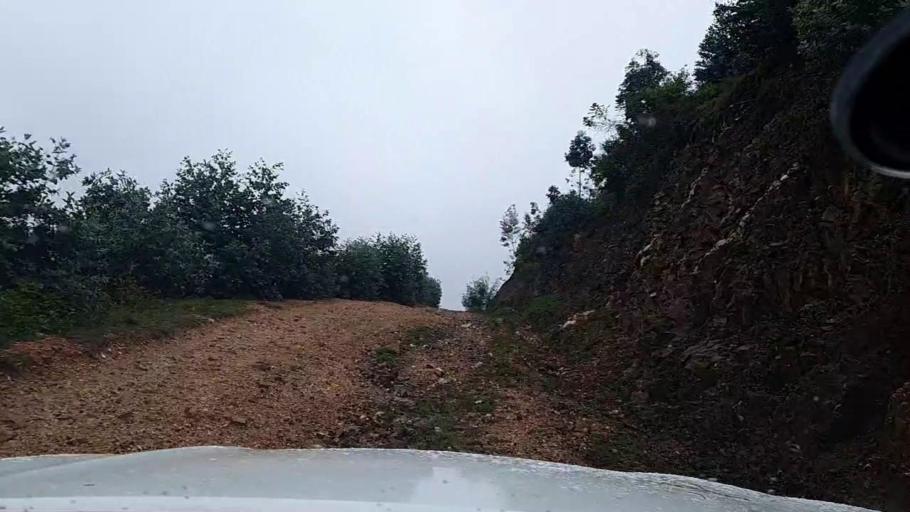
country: RW
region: Western Province
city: Kibuye
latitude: -2.1395
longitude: 29.4582
